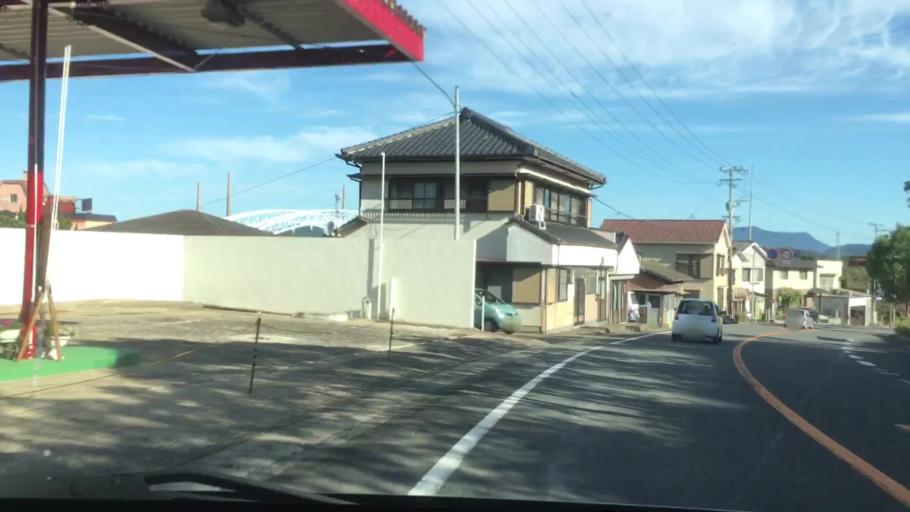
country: JP
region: Nagasaki
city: Sasebo
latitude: 33.0506
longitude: 129.7557
